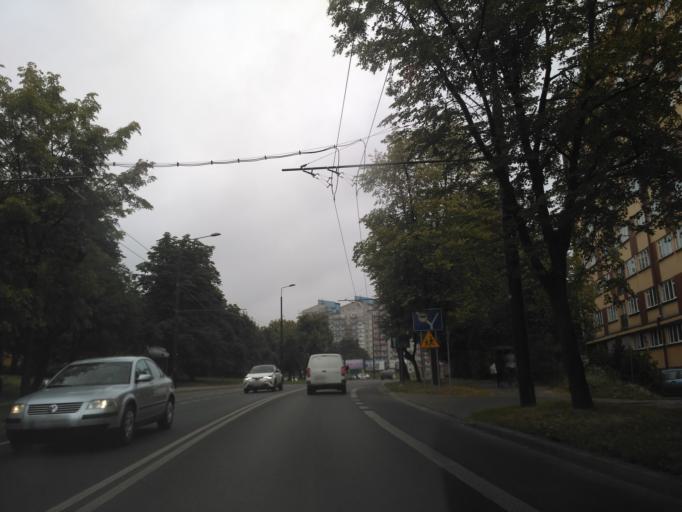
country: PL
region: Lublin Voivodeship
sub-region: Powiat lubelski
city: Lublin
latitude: 51.2550
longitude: 22.5751
